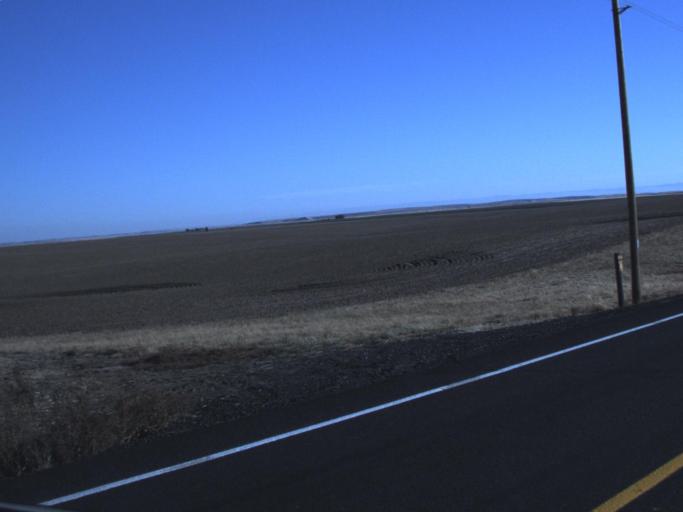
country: US
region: Washington
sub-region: Adams County
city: Ritzville
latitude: 46.9718
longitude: -118.3434
